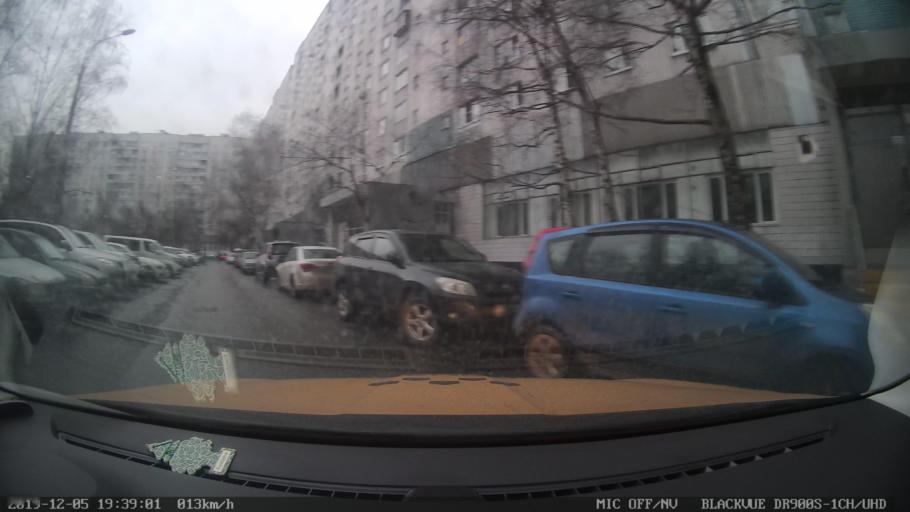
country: RU
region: Moscow
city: Lianozovo
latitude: 55.8946
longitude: 37.5906
